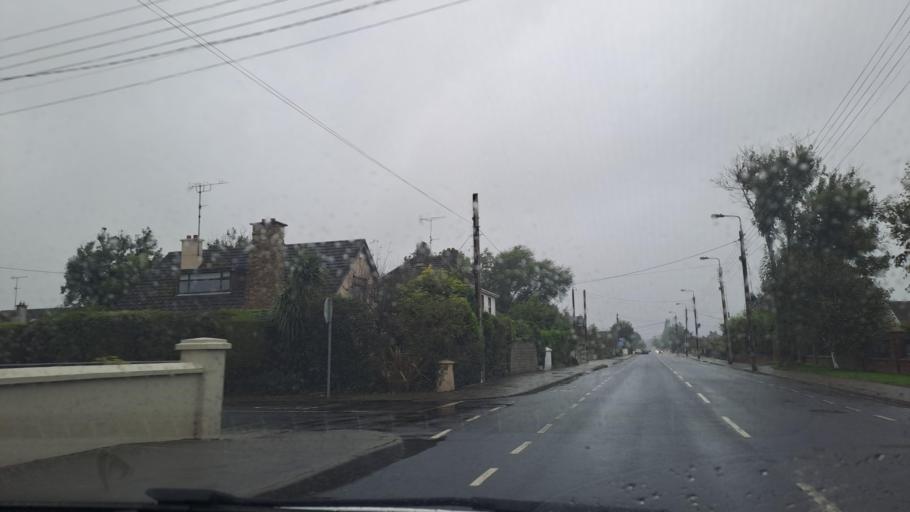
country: IE
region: Leinster
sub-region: Lu
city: Dundalk
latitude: 53.9946
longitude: -6.3869
